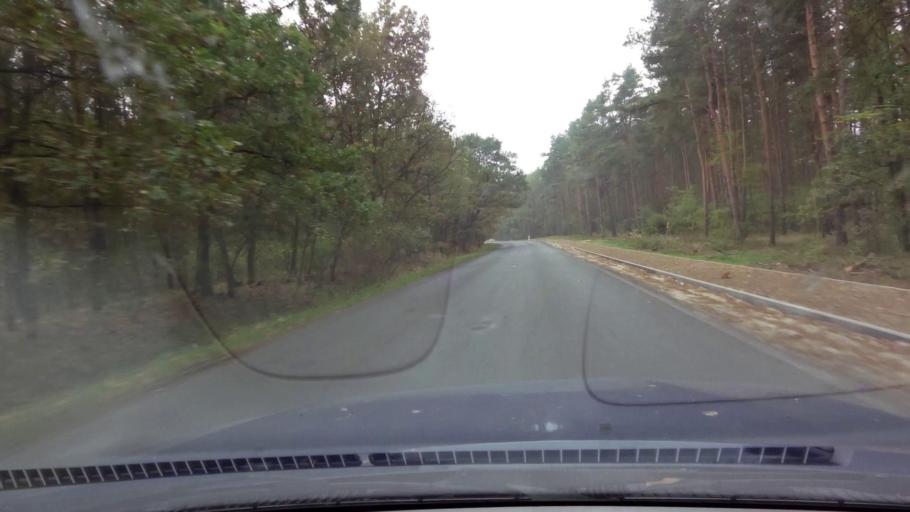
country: PL
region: West Pomeranian Voivodeship
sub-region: Powiat goleniowski
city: Goleniow
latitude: 53.5331
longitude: 14.7600
